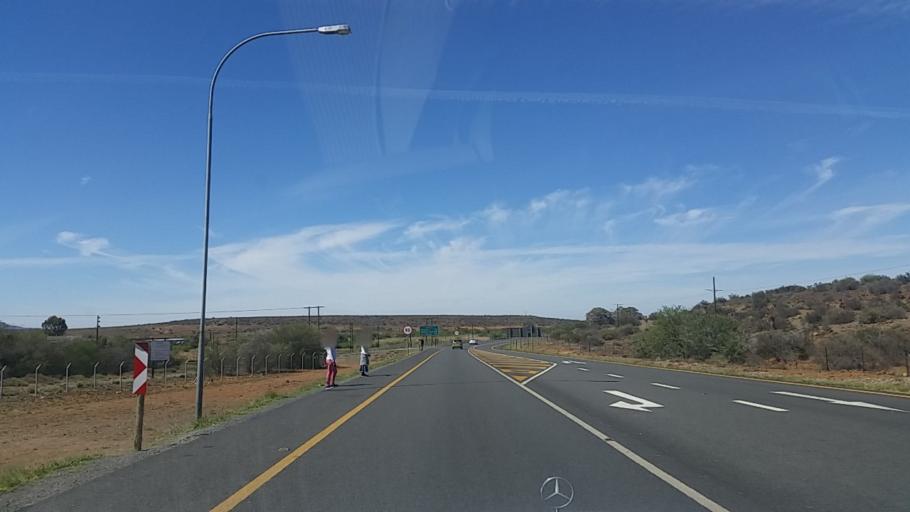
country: ZA
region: Eastern Cape
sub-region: Cacadu District Municipality
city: Graaff-Reinet
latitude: -32.2721
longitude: 24.5454
